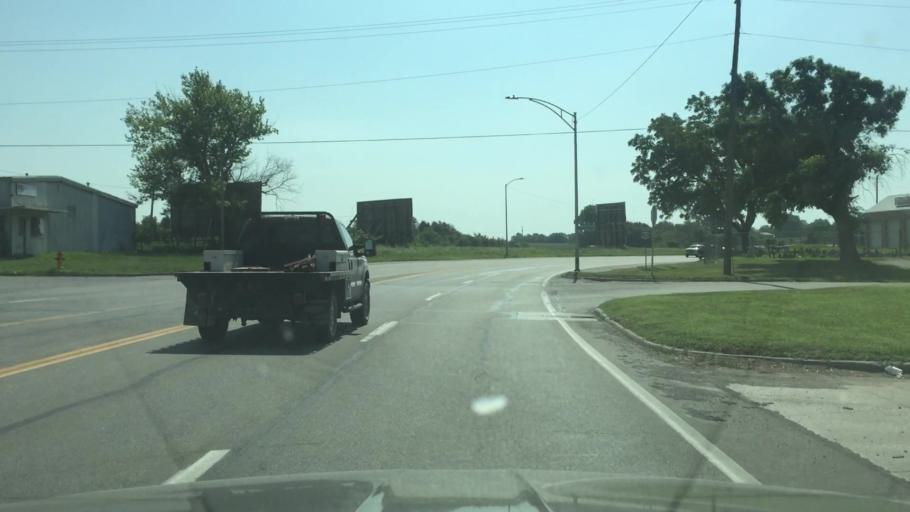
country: US
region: Missouri
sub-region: Pettis County
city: Sedalia
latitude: 38.7030
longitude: -93.1950
